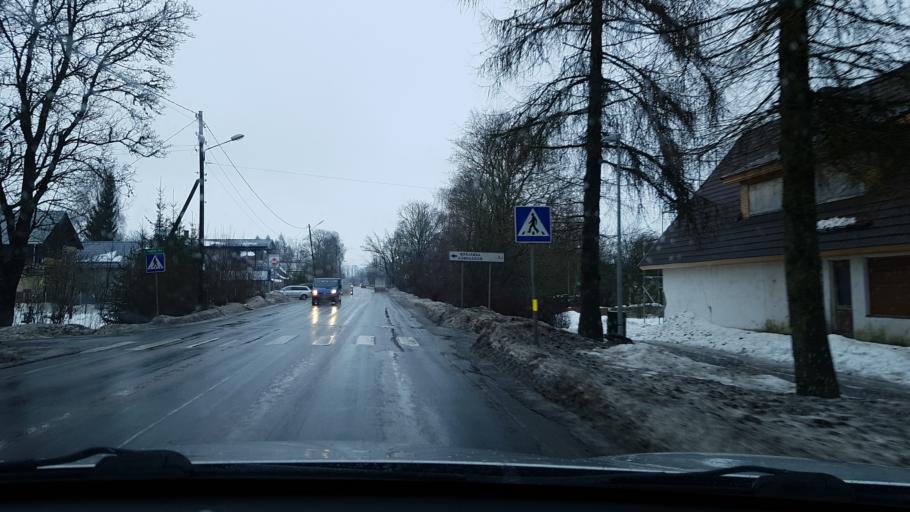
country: EE
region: Raplamaa
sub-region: Maerjamaa vald
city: Marjamaa
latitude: 58.9060
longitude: 24.4295
